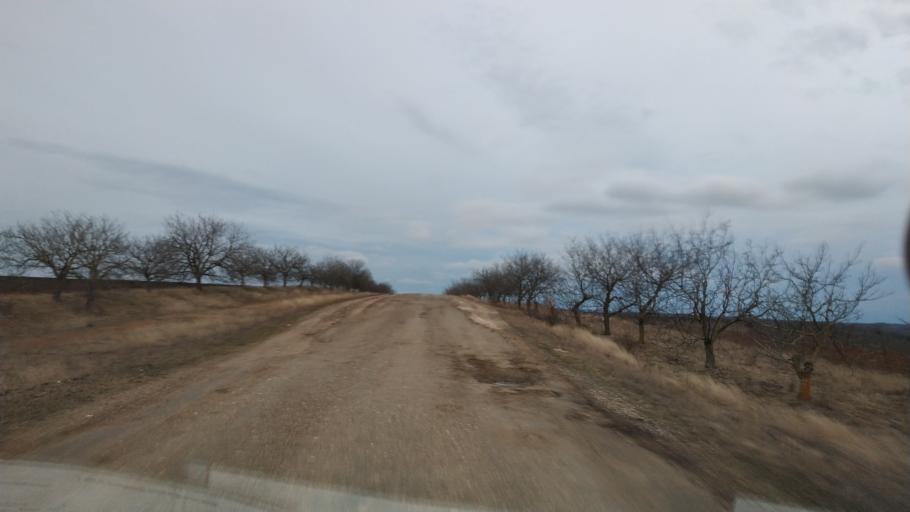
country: MD
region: Causeni
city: Causeni
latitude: 46.5754
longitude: 29.3896
